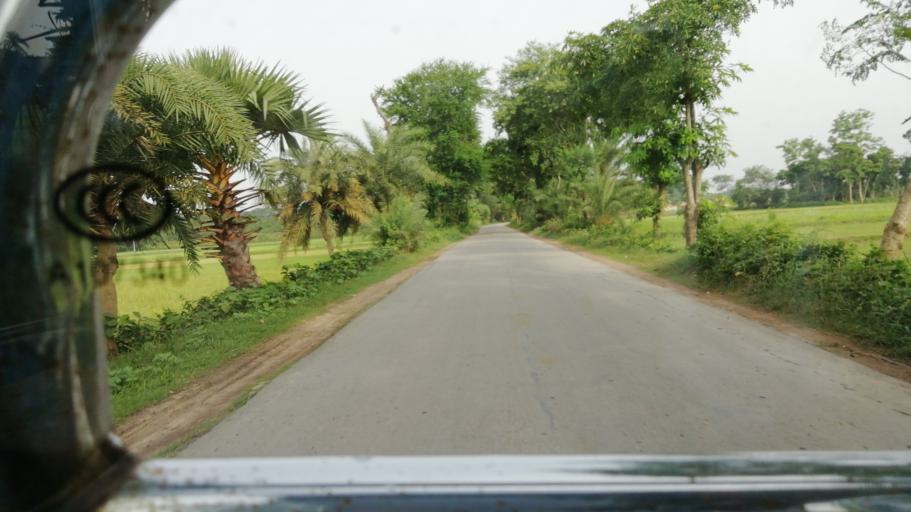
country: BD
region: Khulna
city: Kesabpur
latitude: 23.0259
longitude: 89.2534
